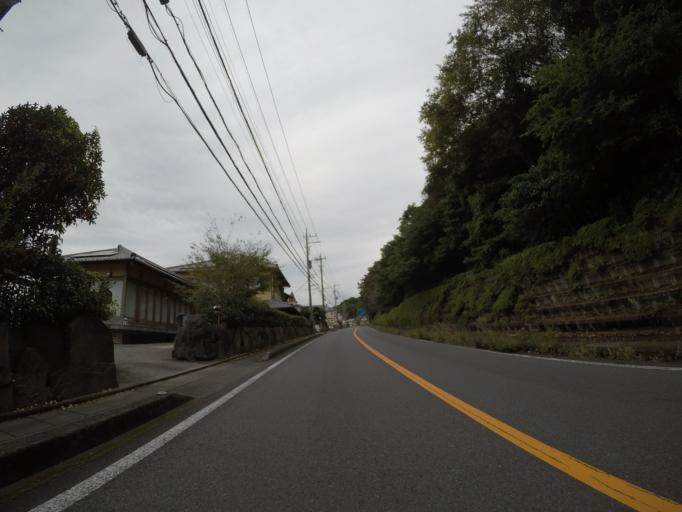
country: JP
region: Shizuoka
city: Fuji
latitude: 35.1925
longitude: 138.6823
